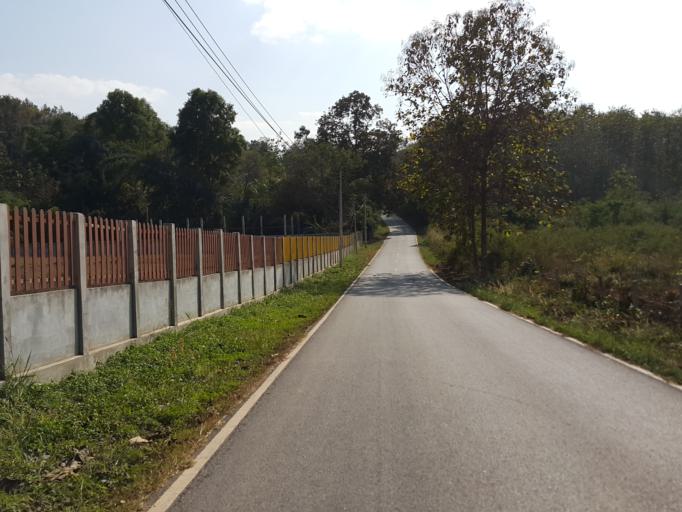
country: TH
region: Chiang Mai
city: Mae On
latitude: 18.8149
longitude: 99.2383
